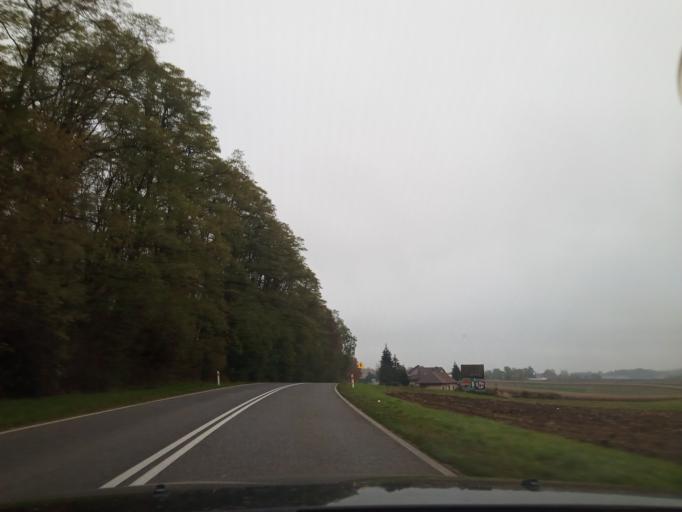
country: PL
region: Lesser Poland Voivodeship
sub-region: Powiat proszowicki
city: Klimontow
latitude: 50.2340
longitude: 20.3897
